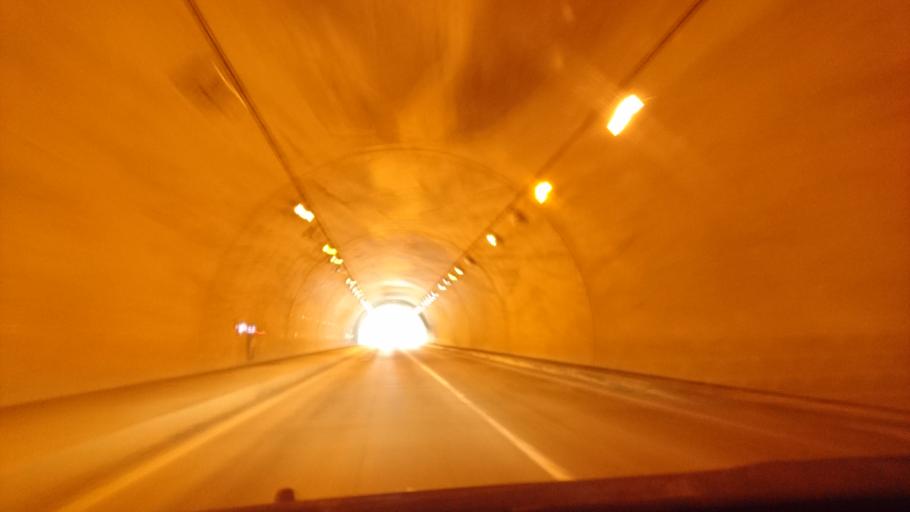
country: JP
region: Iwate
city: Ichinoseki
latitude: 38.9006
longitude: 140.9224
